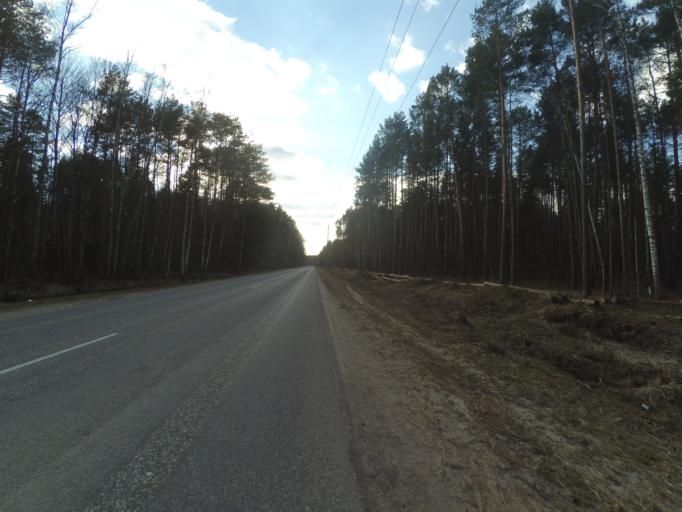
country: RU
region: Moskovskaya
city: Pushchino
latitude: 54.9043
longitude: 37.6824
